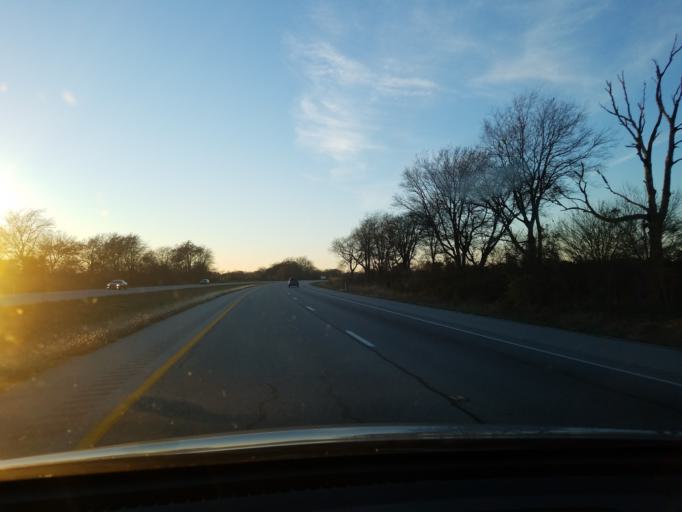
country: US
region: Indiana
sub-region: Posey County
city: Poseyville
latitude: 38.1846
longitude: -87.8154
